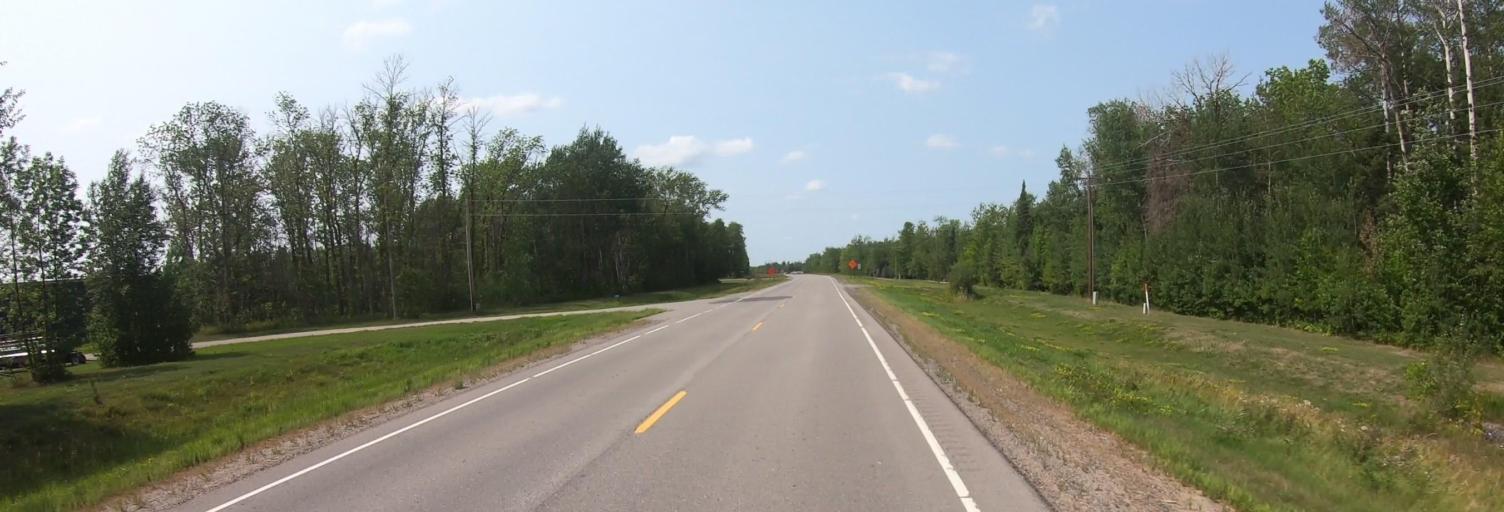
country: US
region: Minnesota
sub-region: Lake of the Woods County
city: Baudette
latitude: 48.6939
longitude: -94.4711
